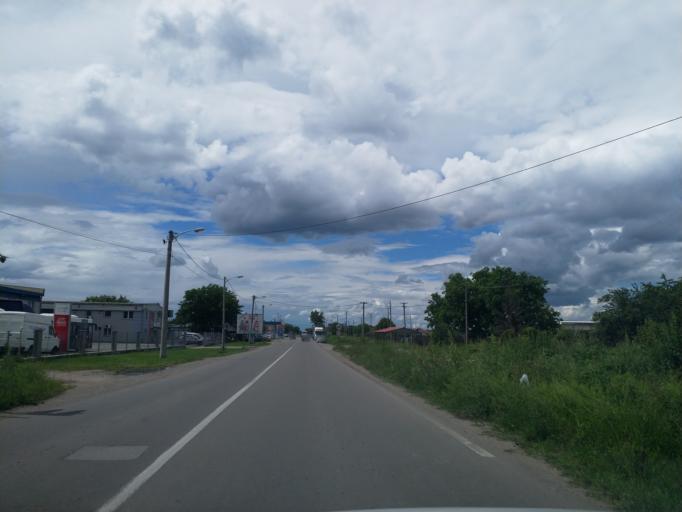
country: RS
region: Central Serbia
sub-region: Pomoravski Okrug
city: Paracin
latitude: 43.8716
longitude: 21.4004
